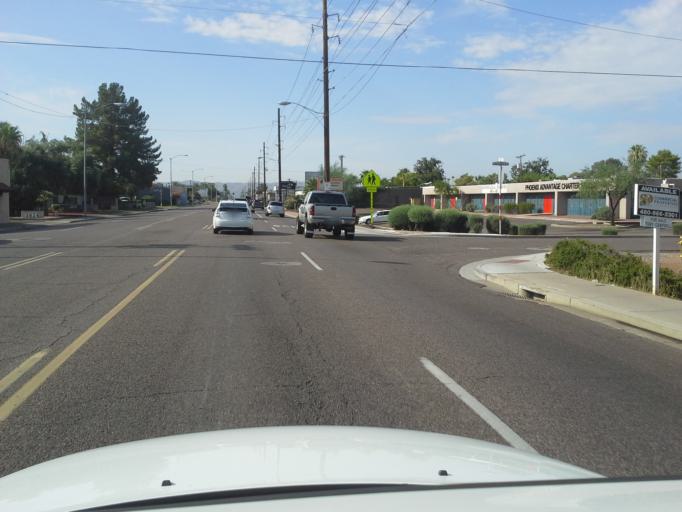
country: US
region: Arizona
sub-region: Maricopa County
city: Phoenix
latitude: 33.4922
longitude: -112.0477
